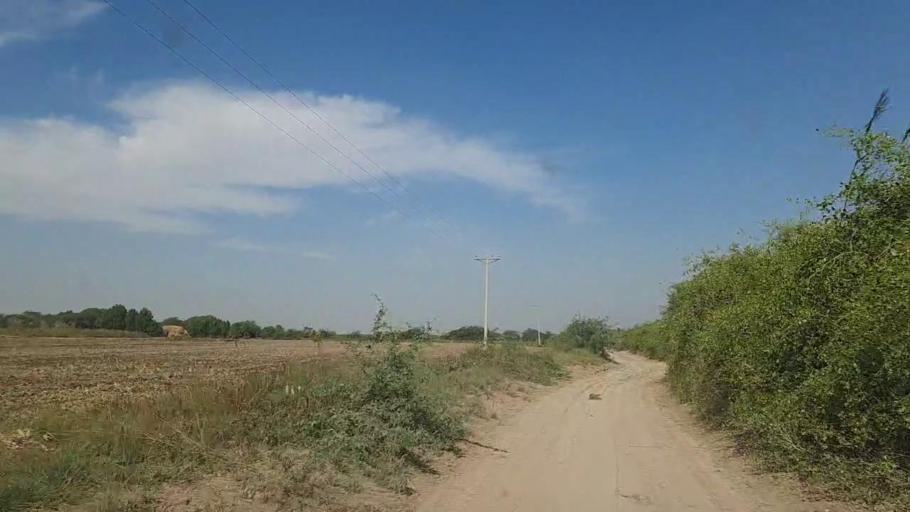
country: PK
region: Sindh
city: Bulri
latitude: 24.8282
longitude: 68.2711
